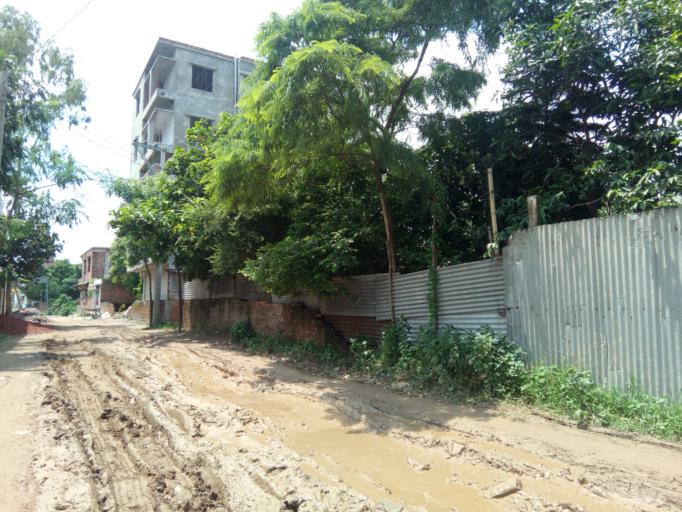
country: BD
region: Dhaka
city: Azimpur
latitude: 23.7346
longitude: 90.3403
